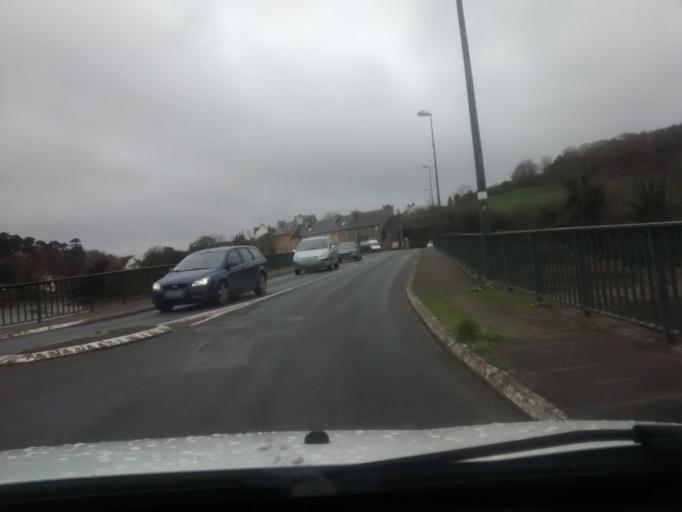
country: FR
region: Brittany
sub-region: Departement des Cotes-d'Armor
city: Treguier
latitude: 48.7909
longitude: -3.2303
